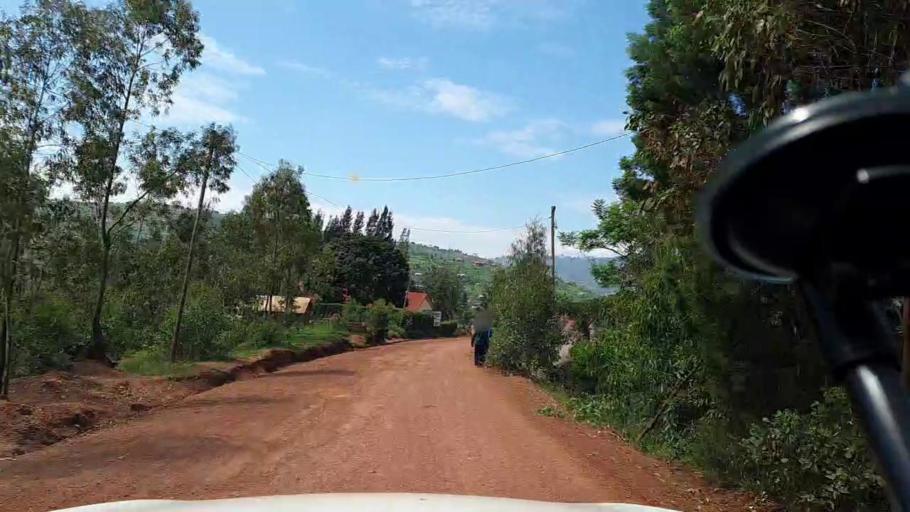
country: RW
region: Kigali
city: Kigali
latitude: -1.7992
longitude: 29.8962
